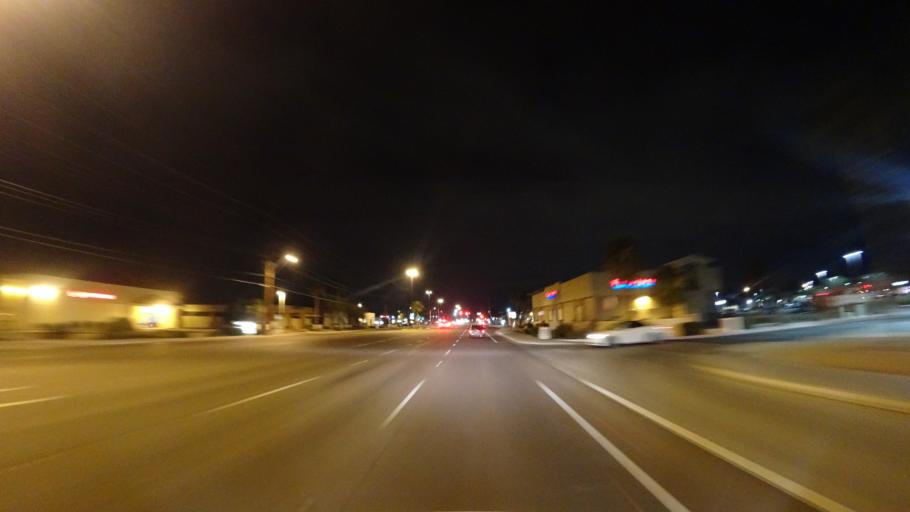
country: US
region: Arizona
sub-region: Maricopa County
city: Gilbert
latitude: 33.3646
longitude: -111.7876
